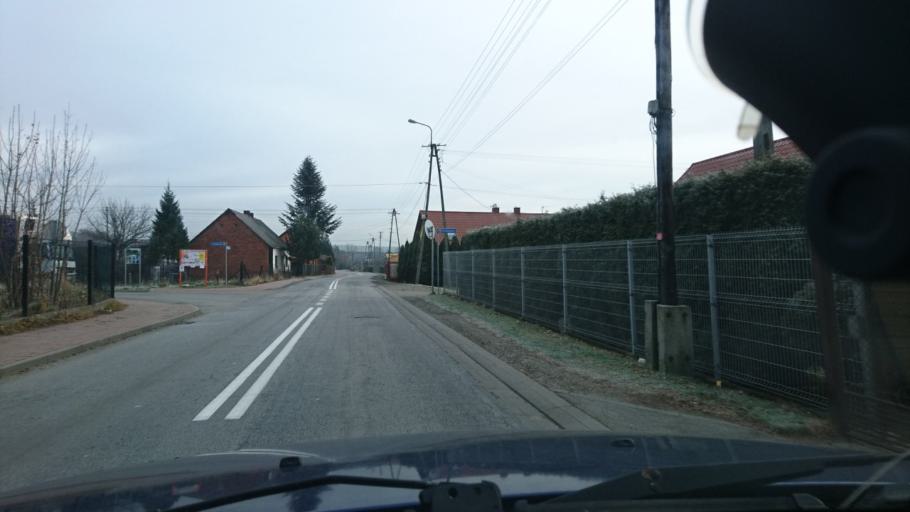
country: PL
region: Silesian Voivodeship
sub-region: Powiat bielski
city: Rybarzowice
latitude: 49.7290
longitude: 19.1109
